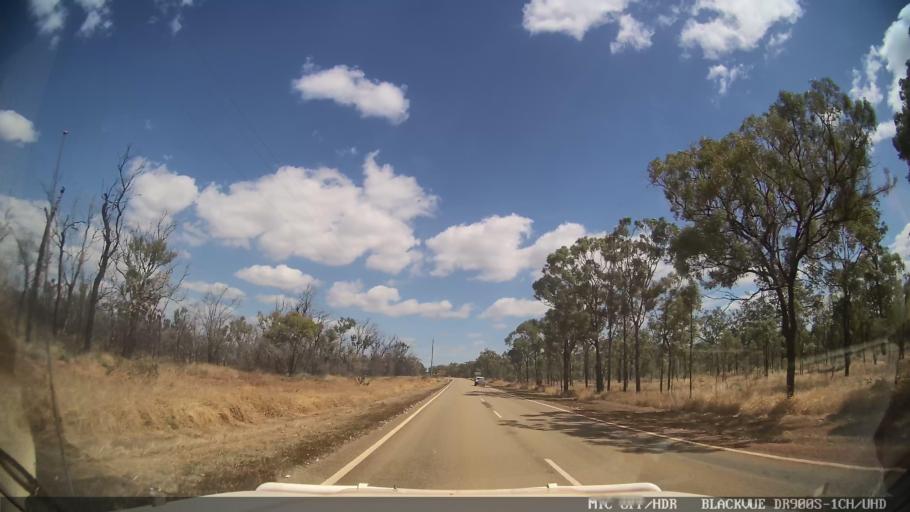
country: AU
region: Queensland
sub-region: Tablelands
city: Ravenshoe
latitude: -18.1322
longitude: 144.8147
